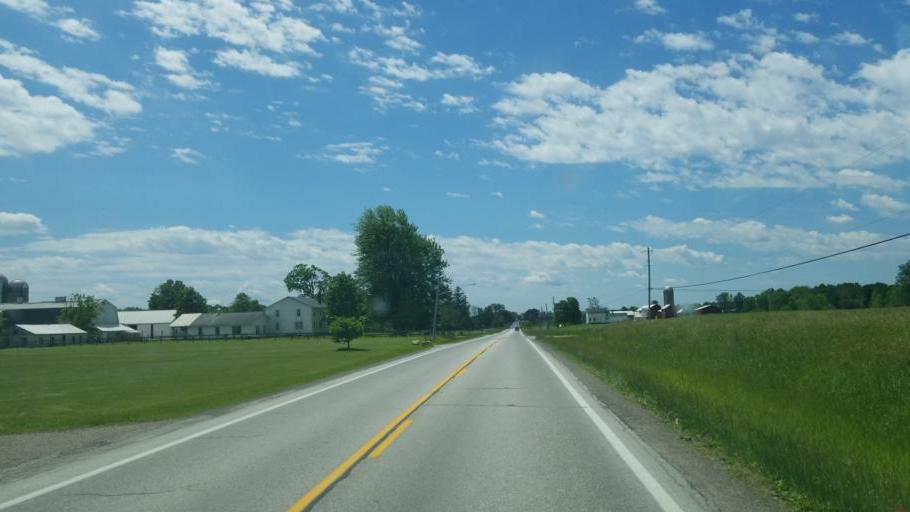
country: US
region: Ohio
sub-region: Geauga County
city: Middlefield
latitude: 41.4435
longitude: -80.9551
